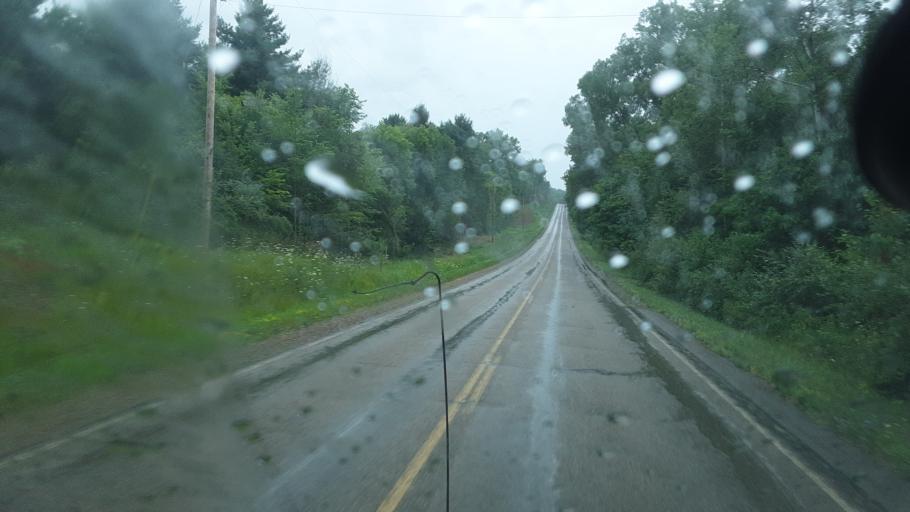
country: US
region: Ohio
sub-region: Williams County
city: Pioneer
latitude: 41.7086
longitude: -84.6790
